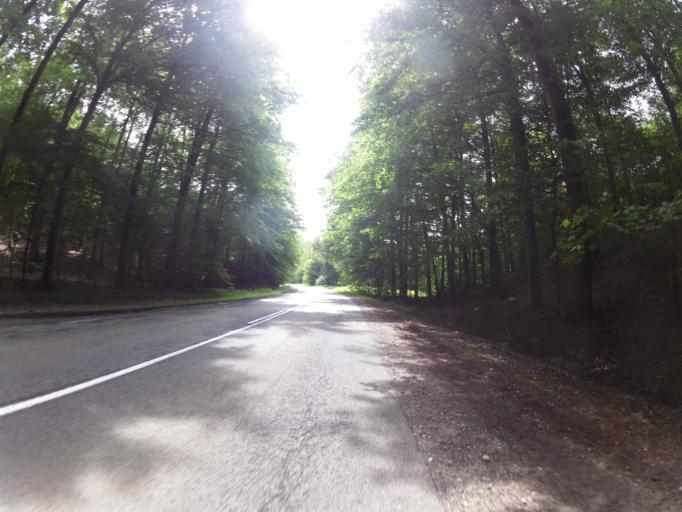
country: DK
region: North Denmark
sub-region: Bronderslev Kommune
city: Dronninglund
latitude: 57.2032
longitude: 10.2757
